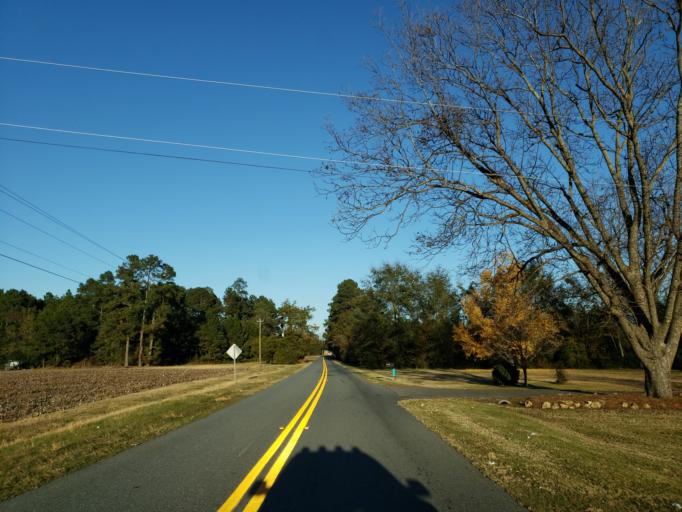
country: US
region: Georgia
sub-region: Dooly County
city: Unadilla
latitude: 32.1884
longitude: -83.7708
